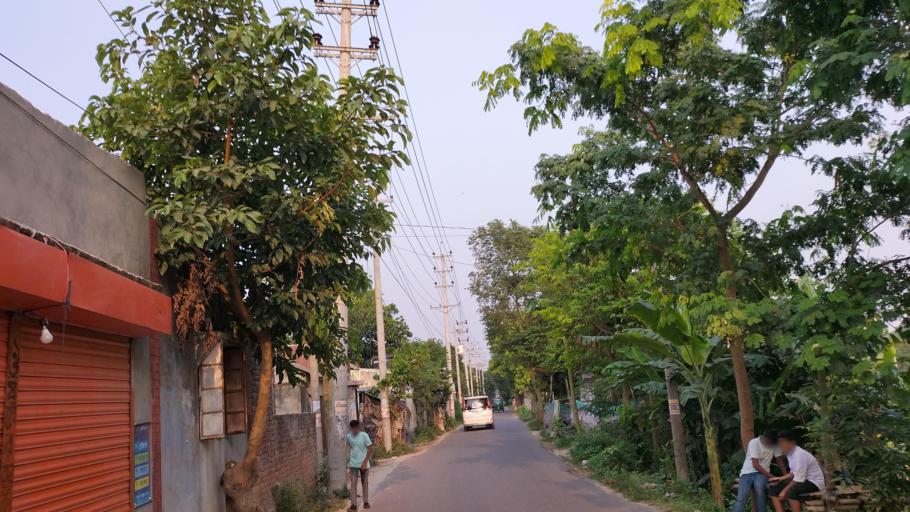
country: BD
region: Dhaka
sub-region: Dhaka
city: Dhaka
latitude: 23.6549
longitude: 90.3417
